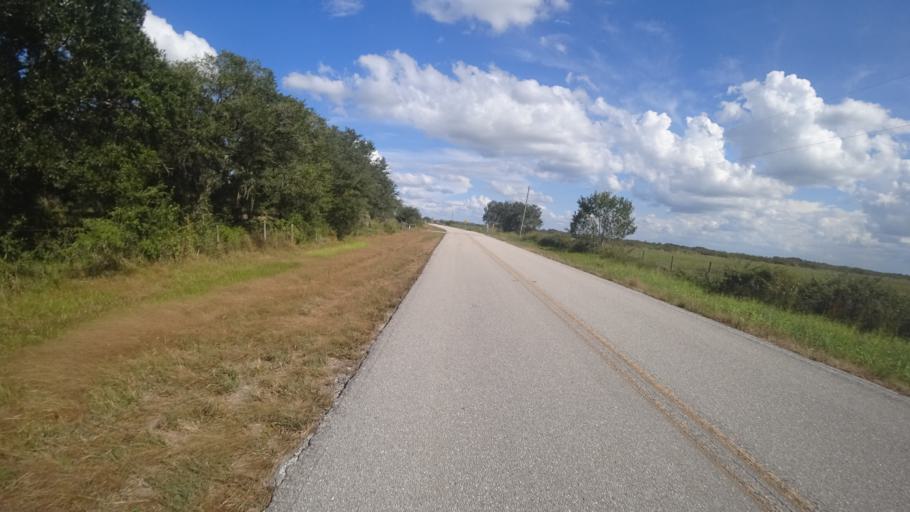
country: US
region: Florida
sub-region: DeSoto County
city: Nocatee
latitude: 27.2688
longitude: -82.0896
